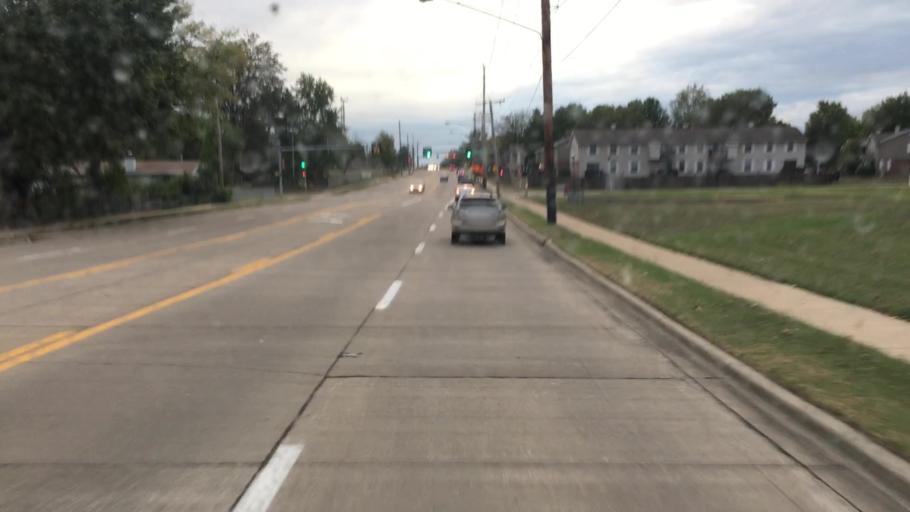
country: US
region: Missouri
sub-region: Saint Louis County
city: Florissant
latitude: 38.8217
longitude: -90.3399
